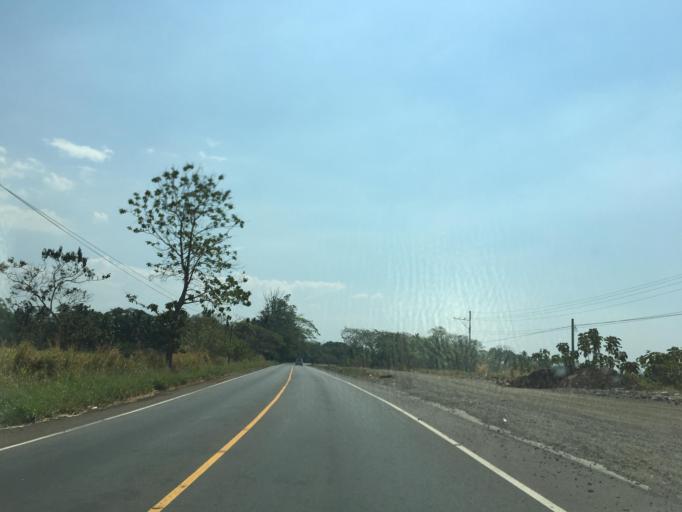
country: GT
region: Escuintla
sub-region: Municipio de Escuintla
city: Escuintla
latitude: 14.2727
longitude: -90.7574
